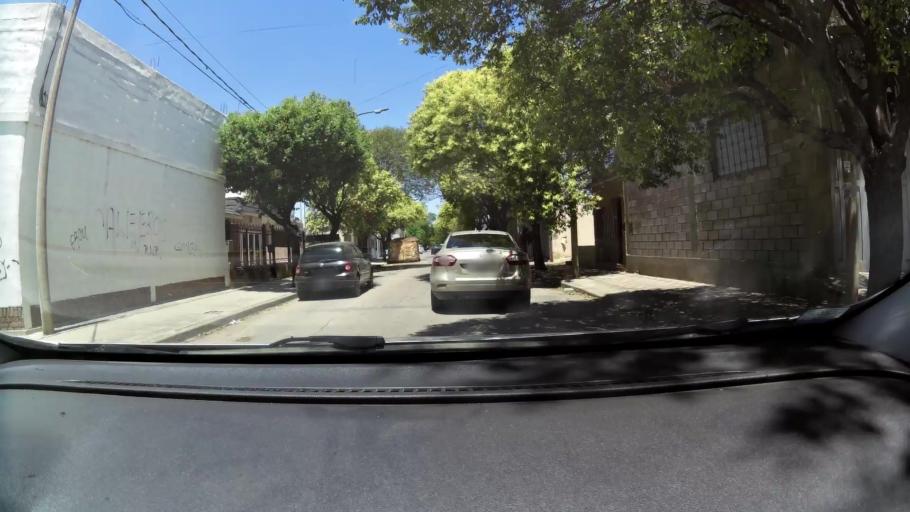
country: AR
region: Cordoba
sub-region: Departamento de Capital
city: Cordoba
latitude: -31.3815
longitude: -64.1356
